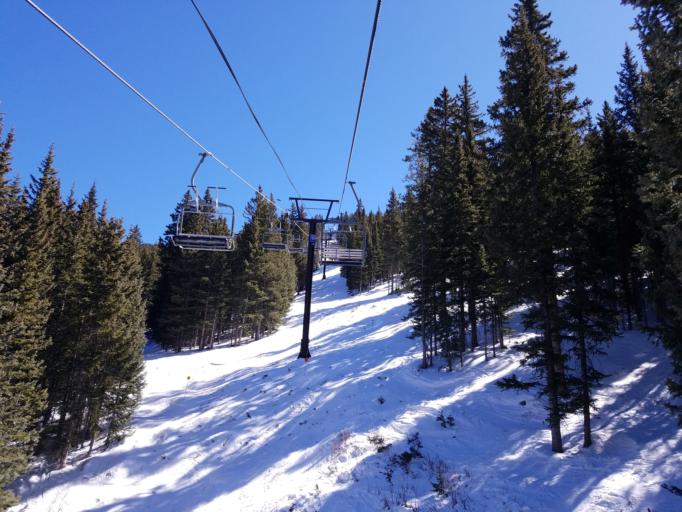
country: US
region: New Mexico
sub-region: Santa Fe County
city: Santa Fe
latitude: 35.7911
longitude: -105.7938
